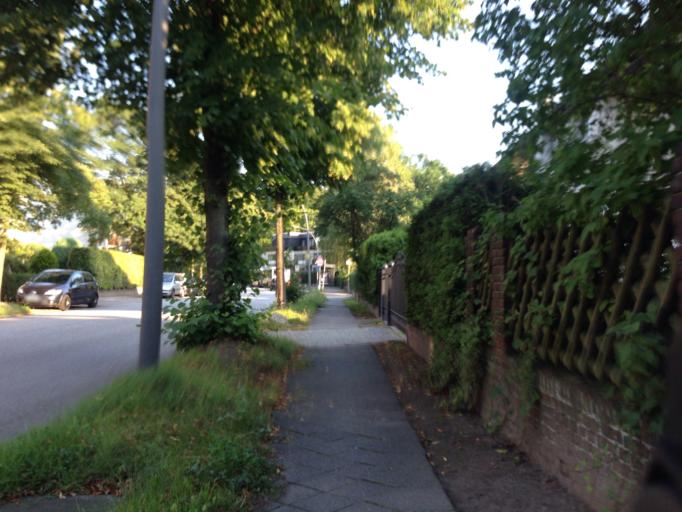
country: DE
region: Hamburg
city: Marienthal
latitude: 53.5699
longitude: 10.0840
